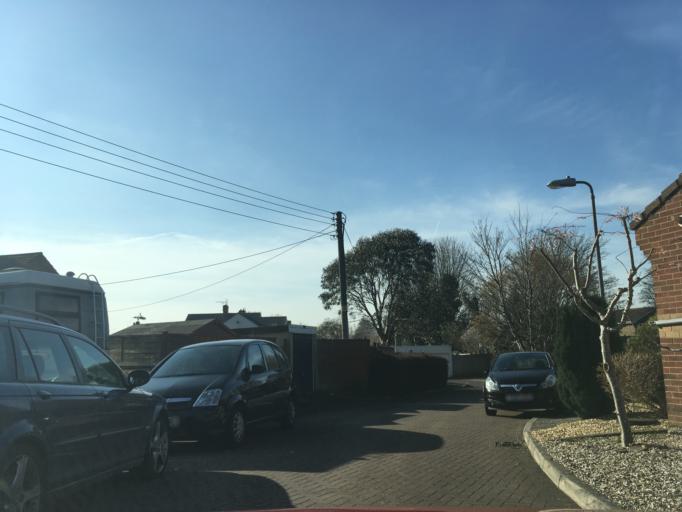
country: GB
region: England
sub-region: South Gloucestershire
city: Chipping Sodbury
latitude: 51.5450
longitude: -2.4036
